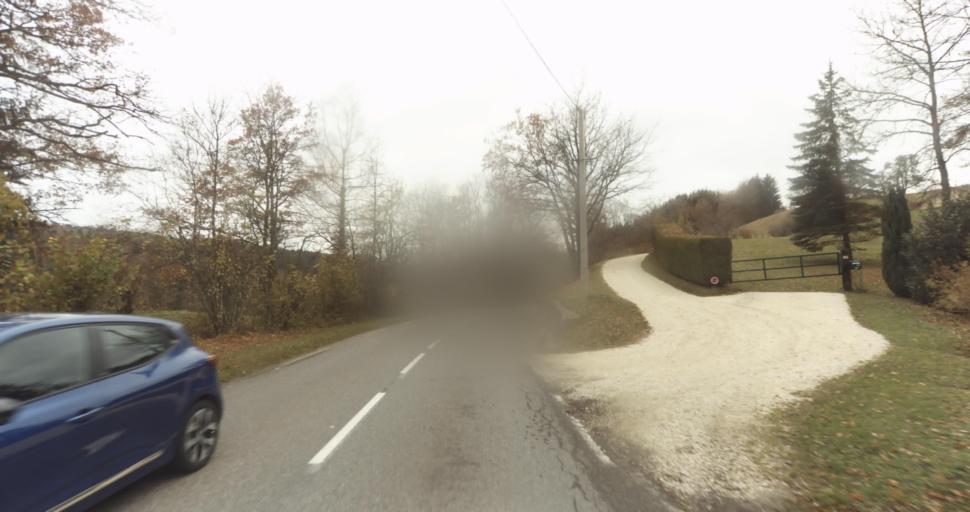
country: FR
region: Rhone-Alpes
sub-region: Departement de la Haute-Savoie
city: Thorens-Glieres
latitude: 45.9994
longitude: 6.2148
